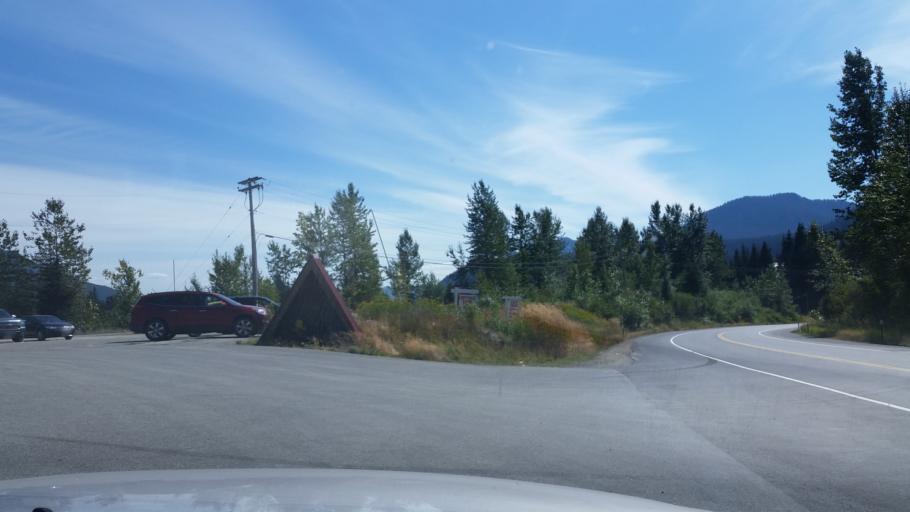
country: US
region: Washington
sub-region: King County
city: Tanner
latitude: 47.4209
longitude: -121.4116
